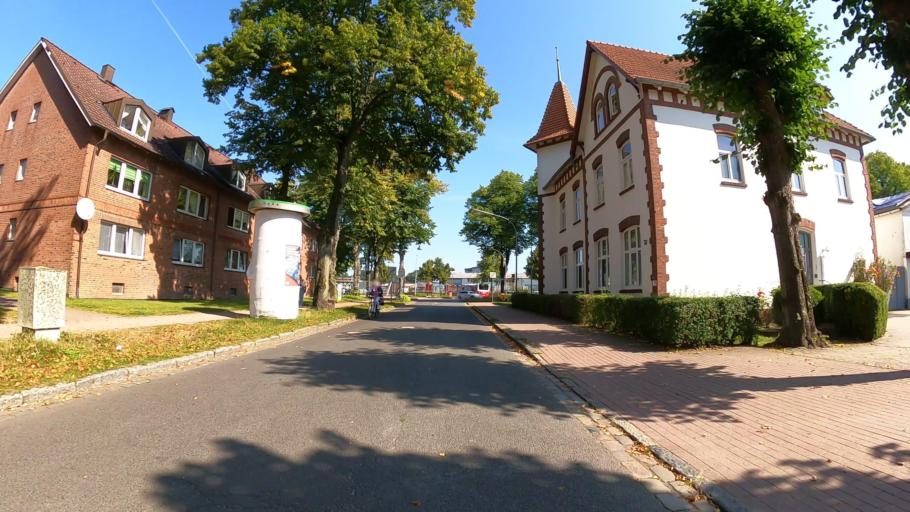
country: DE
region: Schleswig-Holstein
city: Bad Bramstedt
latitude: 53.9204
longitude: 9.8883
